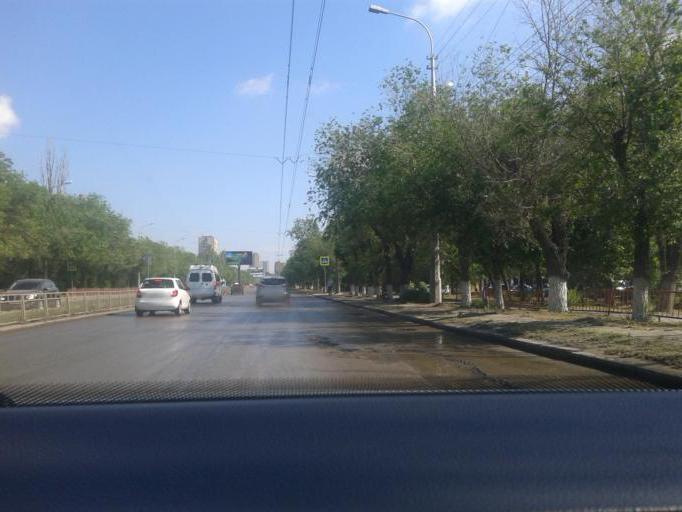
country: RU
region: Volgograd
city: Volgograd
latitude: 48.6090
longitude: 44.4225
